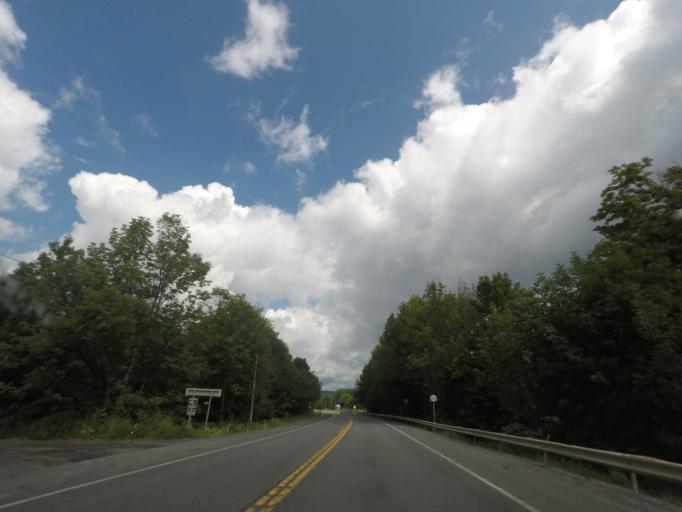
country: US
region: Massachusetts
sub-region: Berkshire County
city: Williamstown
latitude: 42.6344
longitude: -73.3587
